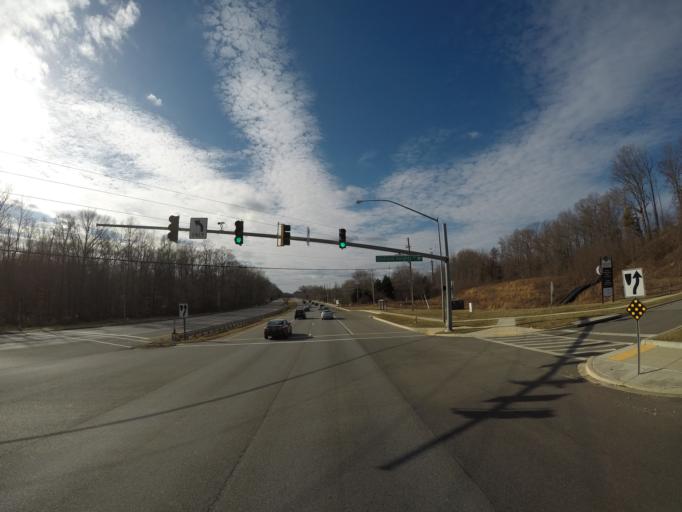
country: US
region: Maryland
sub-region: Charles County
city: Waldorf
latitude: 38.6527
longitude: -76.9724
